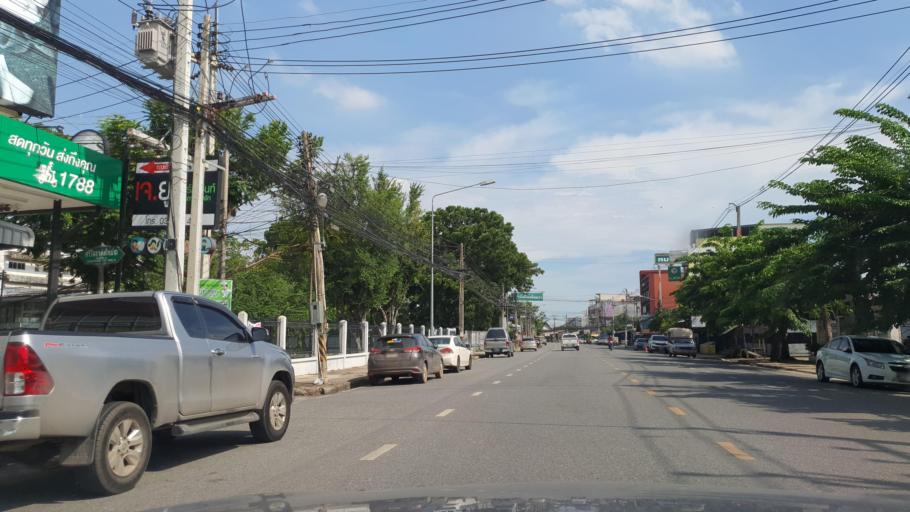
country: TH
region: Chachoengsao
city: Chachoengsao
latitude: 13.6911
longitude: 101.0638
